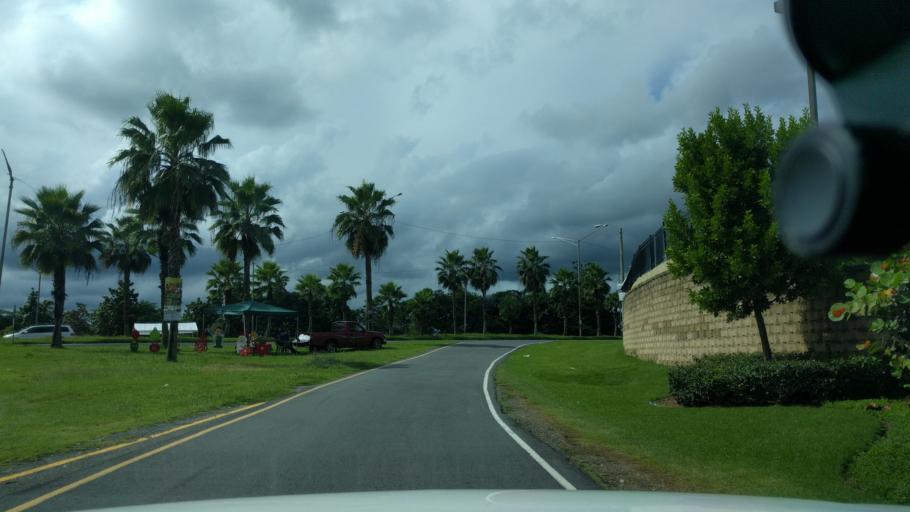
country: PR
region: Toa Alta
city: Pajaros
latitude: 18.3399
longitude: -66.2026
